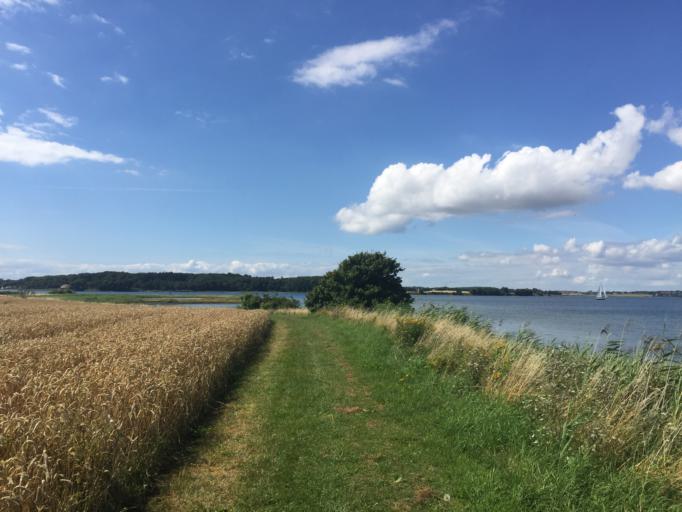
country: DK
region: South Denmark
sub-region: Faaborg-Midtfyn Kommune
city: Faaborg
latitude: 55.0699
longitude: 10.2412
